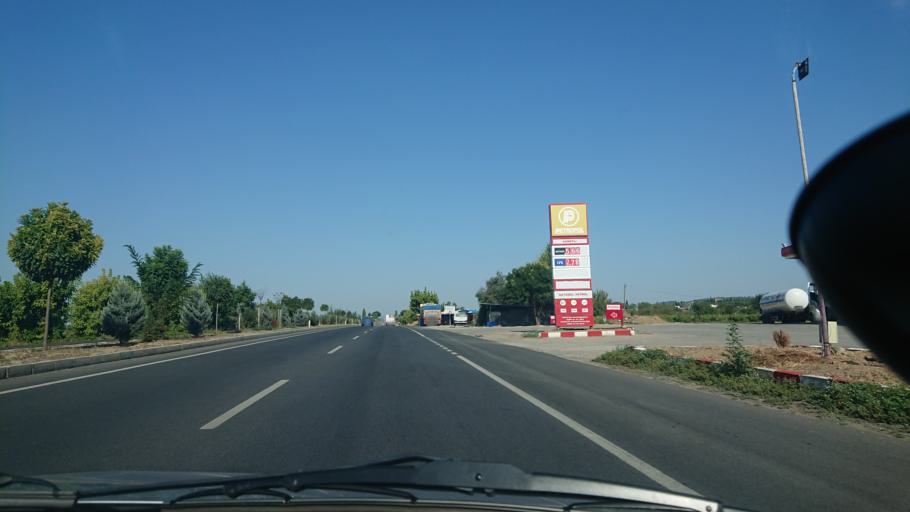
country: TR
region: Manisa
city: Ahmetli
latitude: 38.4966
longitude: 27.8602
